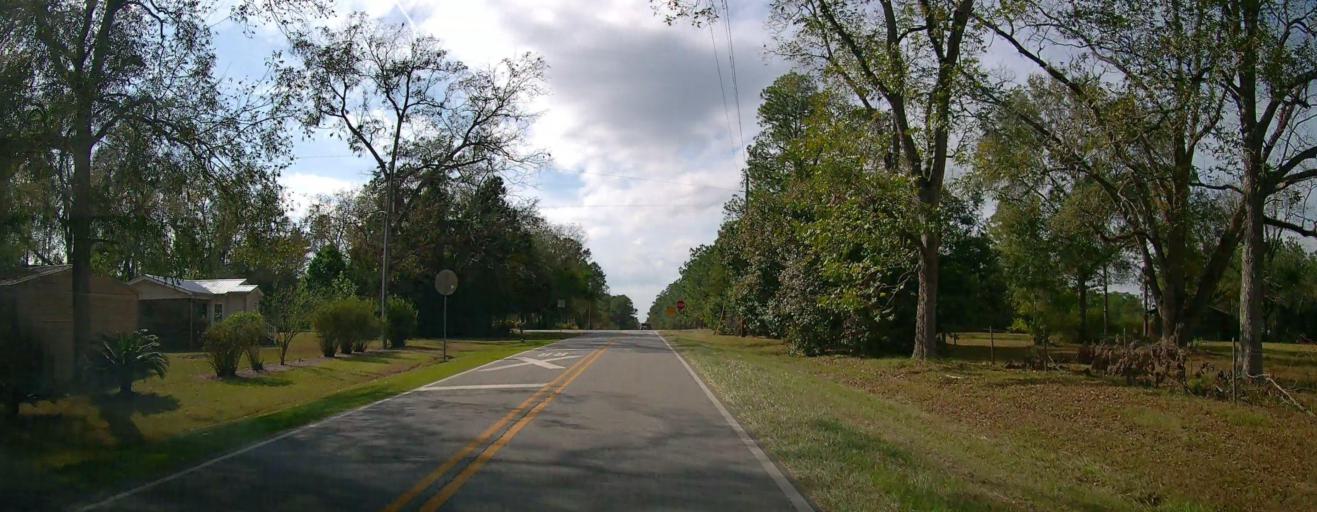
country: US
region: Georgia
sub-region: Thomas County
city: Thomasville
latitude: 30.9497
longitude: -84.0321
